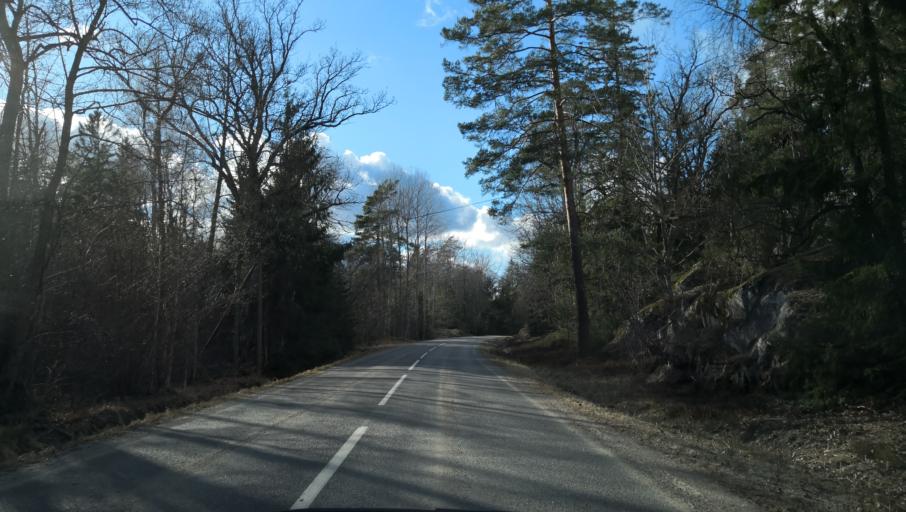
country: SE
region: Stockholm
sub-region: Varmdo Kommun
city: Hemmesta
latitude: 59.2856
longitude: 18.4832
